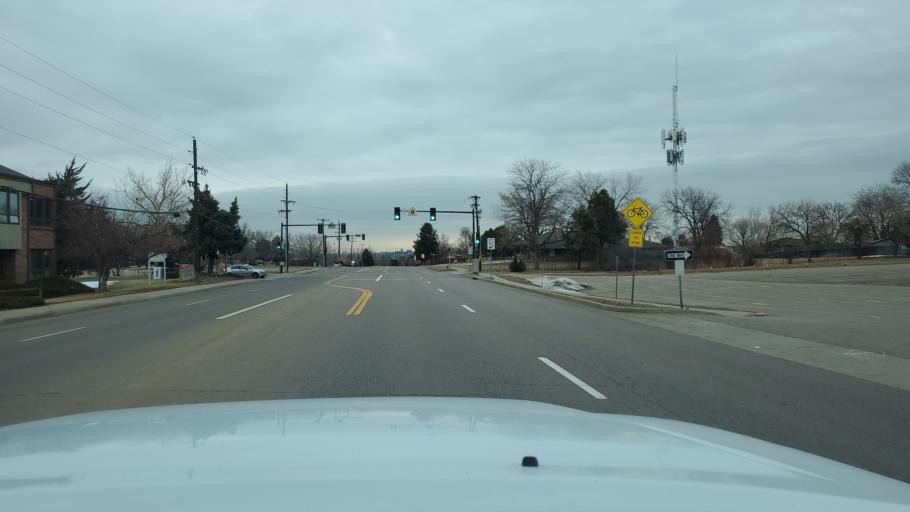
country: US
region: Colorado
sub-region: Arapahoe County
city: Southglenn
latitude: 39.5961
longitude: -104.9414
